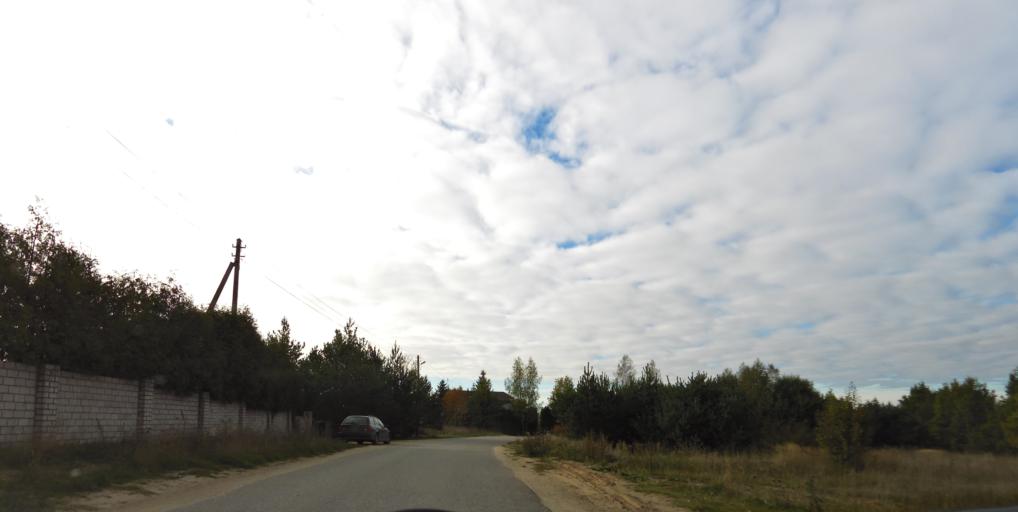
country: LT
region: Vilnius County
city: Pilaite
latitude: 54.7307
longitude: 25.1692
